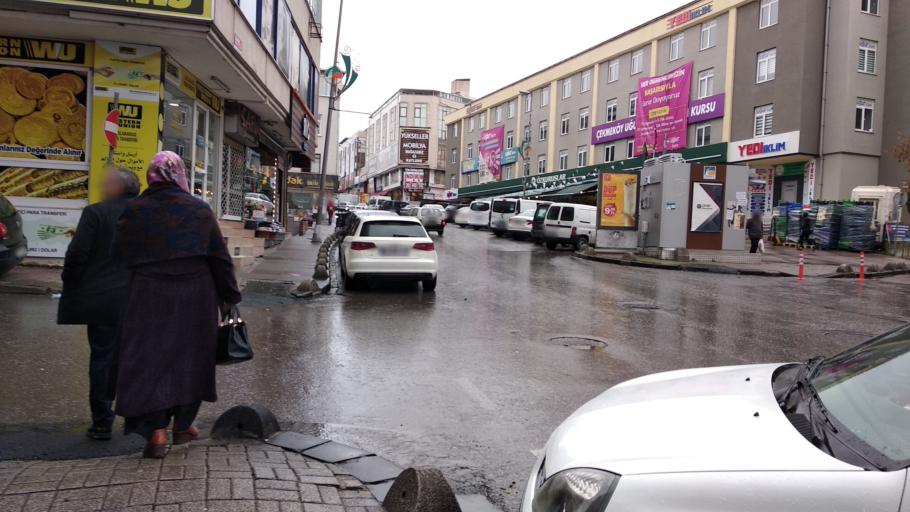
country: TR
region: Istanbul
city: Samandira
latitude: 41.0154
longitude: 29.1903
